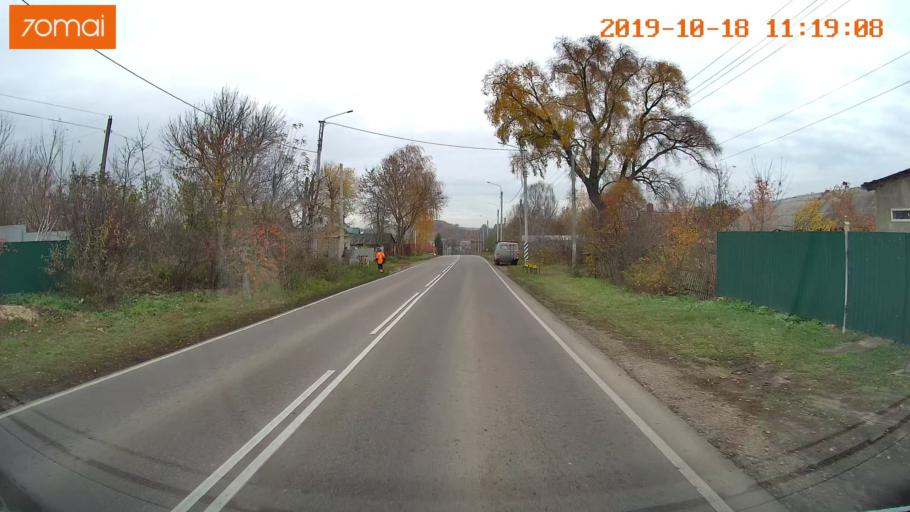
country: RU
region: Tula
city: Kimovsk
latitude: 54.0427
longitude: 38.5517
